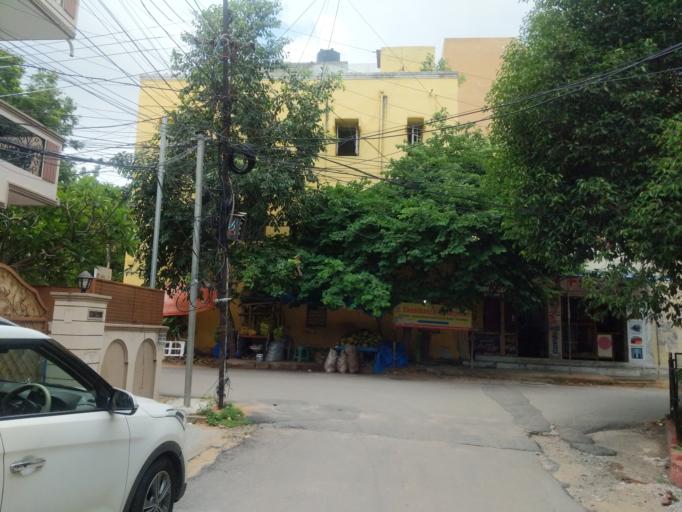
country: IN
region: Telangana
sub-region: Rangareddi
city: Kukatpalli
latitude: 17.4405
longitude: 78.4371
